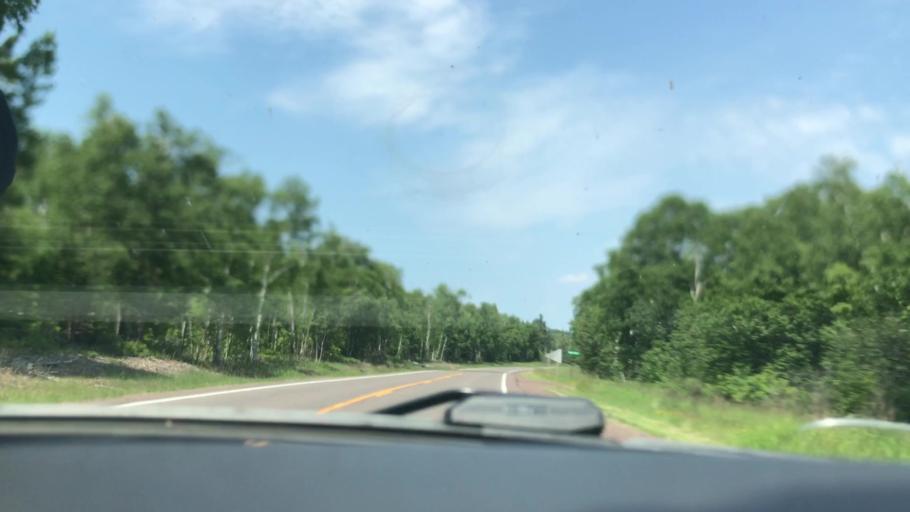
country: US
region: Minnesota
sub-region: Lake County
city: Silver Bay
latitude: 47.4977
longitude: -90.9704
